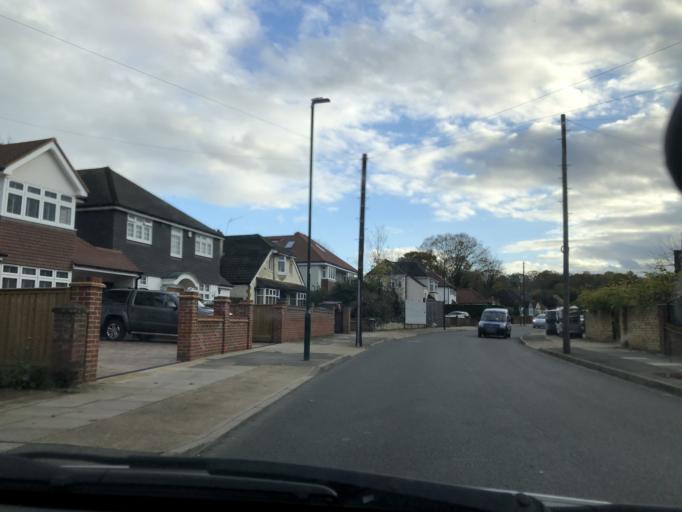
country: GB
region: England
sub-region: Greater London
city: Bexley
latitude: 51.4327
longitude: 0.1660
